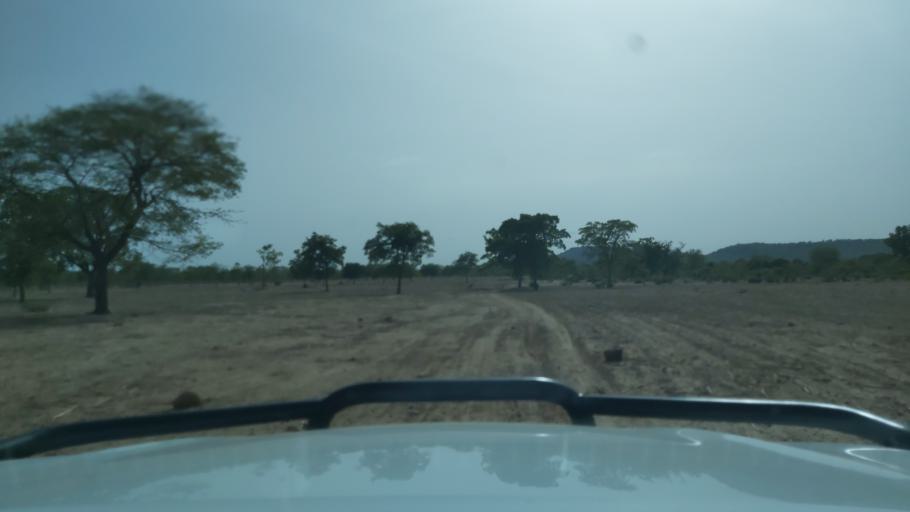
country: ML
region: Koulikoro
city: Koulikoro
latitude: 13.1754
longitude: -7.7468
